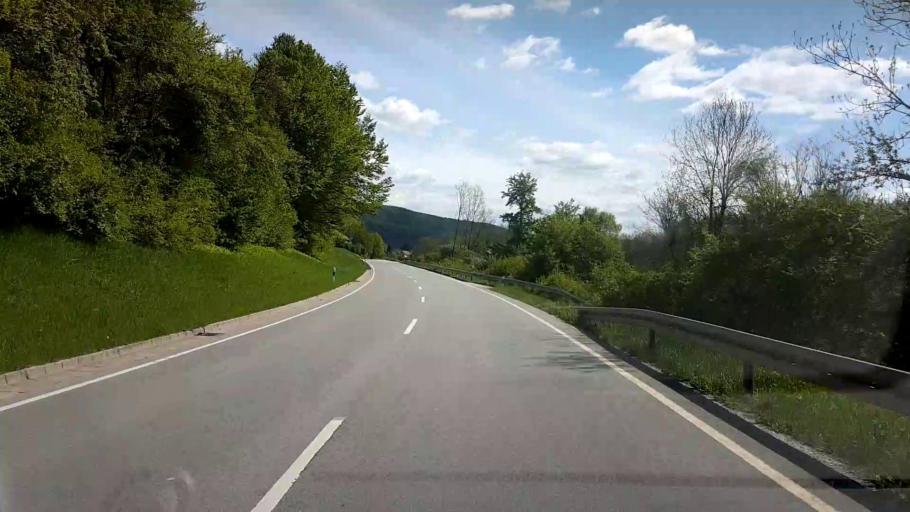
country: DE
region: Bavaria
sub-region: Upper Franconia
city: Ebermannstadt
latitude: 49.7935
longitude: 11.1773
